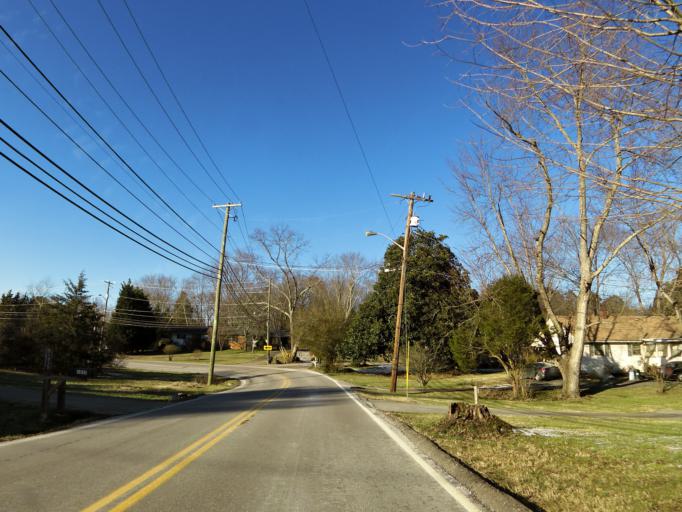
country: US
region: Tennessee
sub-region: Knox County
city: Knoxville
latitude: 35.9447
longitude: -84.0422
